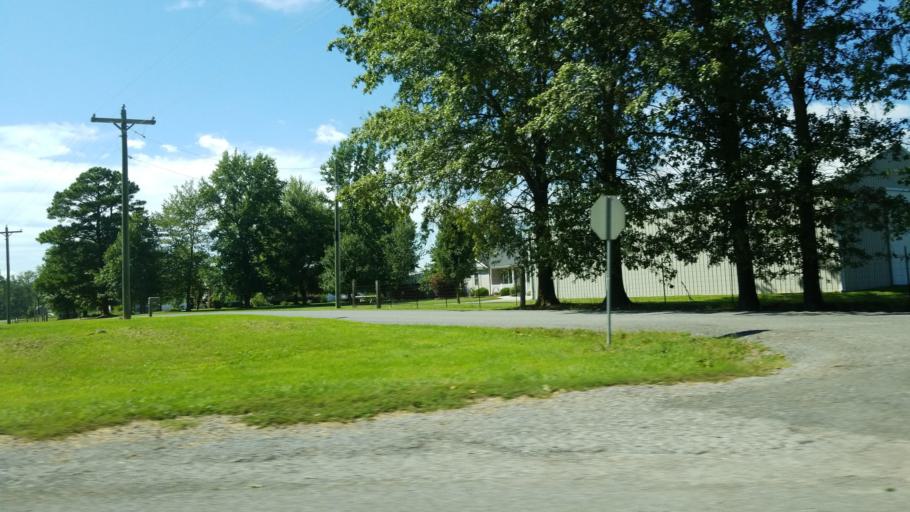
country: US
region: Illinois
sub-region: Williamson County
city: Marion
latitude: 37.7630
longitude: -88.8644
